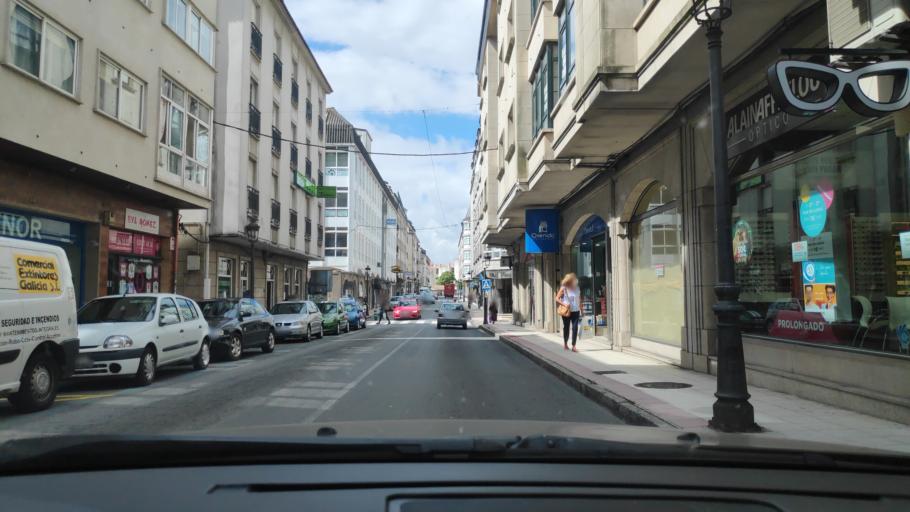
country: ES
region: Galicia
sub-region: Provincia de Pontevedra
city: Caldas de Reis
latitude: 42.6052
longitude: -8.6438
